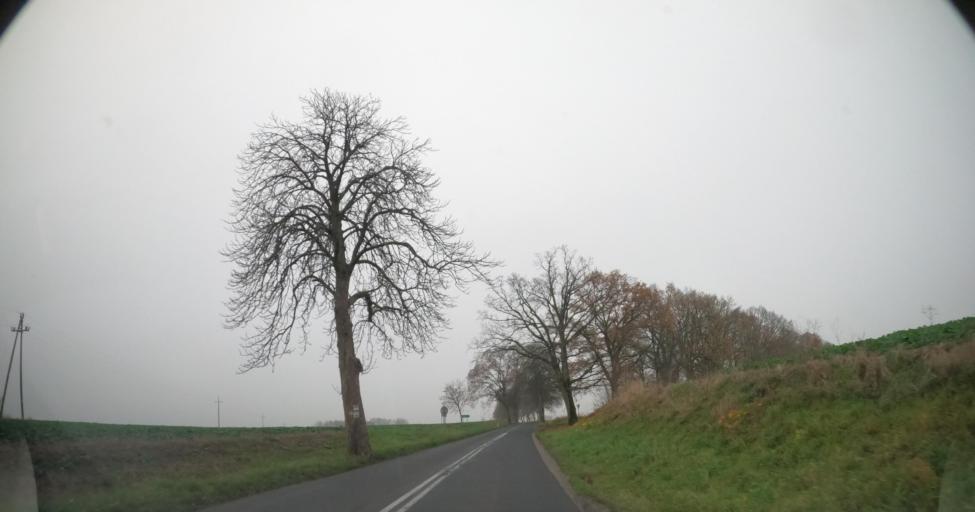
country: PL
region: West Pomeranian Voivodeship
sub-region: Powiat drawski
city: Drawsko Pomorskie
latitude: 53.5843
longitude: 15.7359
